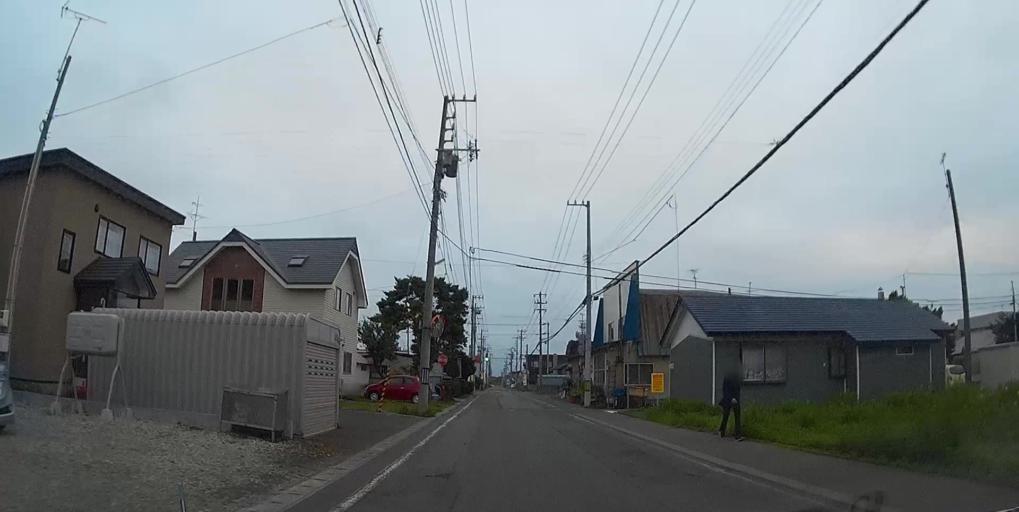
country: JP
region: Hokkaido
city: Nanae
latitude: 42.2579
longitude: 140.2693
